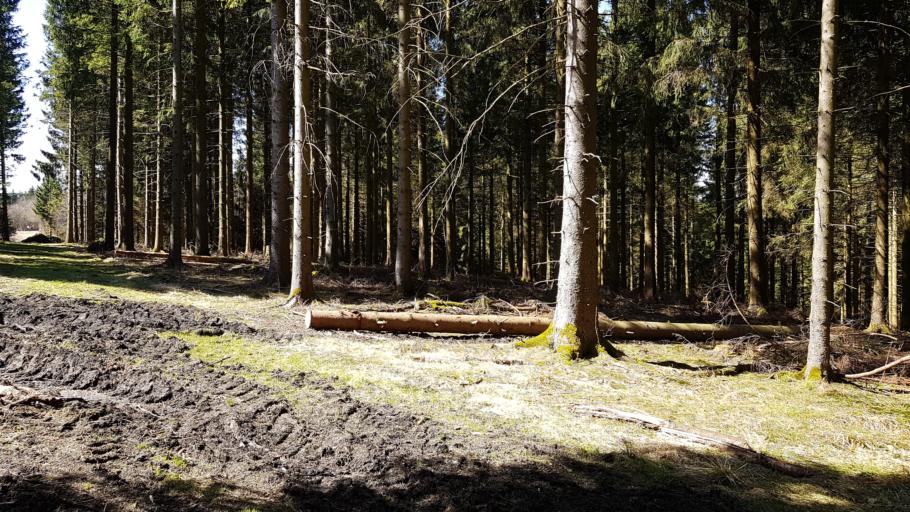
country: DE
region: North Rhine-Westphalia
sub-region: Regierungsbezirk Arnsberg
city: Bad Fredeburg
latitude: 51.2047
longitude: 8.3718
